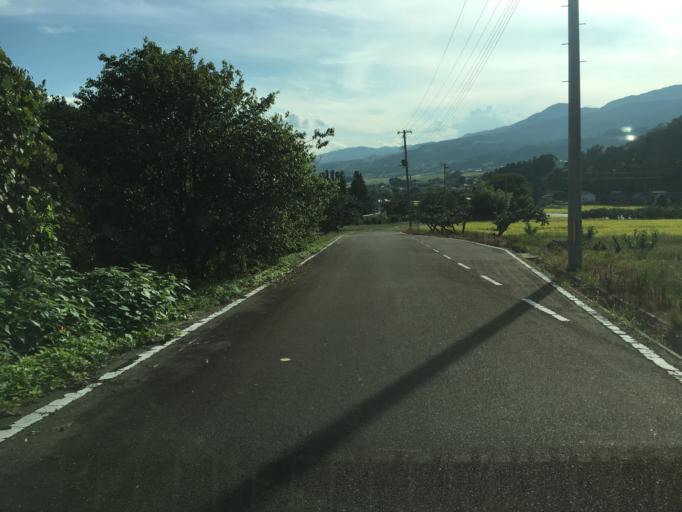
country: JP
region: Fukushima
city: Yanagawamachi-saiwaicho
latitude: 37.8931
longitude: 140.5382
